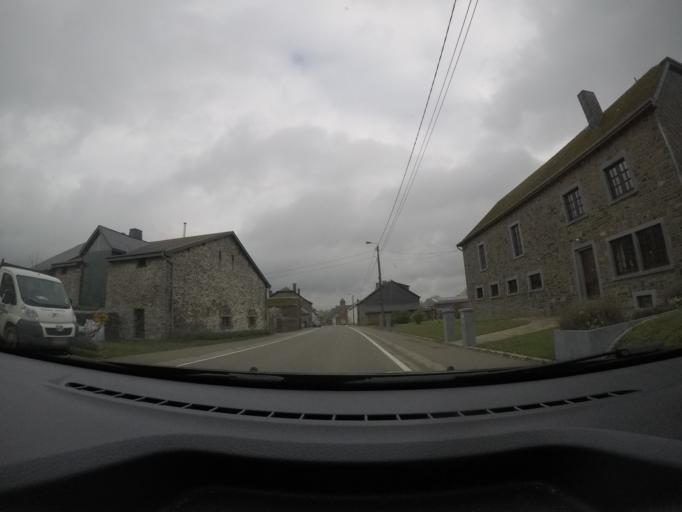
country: BE
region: Wallonia
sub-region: Province du Luxembourg
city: Bertogne
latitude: 50.0854
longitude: 5.7068
